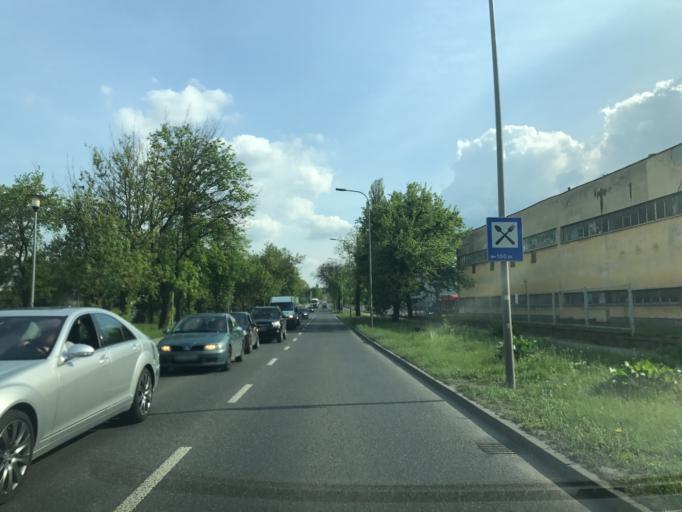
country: PL
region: Kujawsko-Pomorskie
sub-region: Powiat bydgoski
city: Osielsko
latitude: 53.1212
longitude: 18.0874
